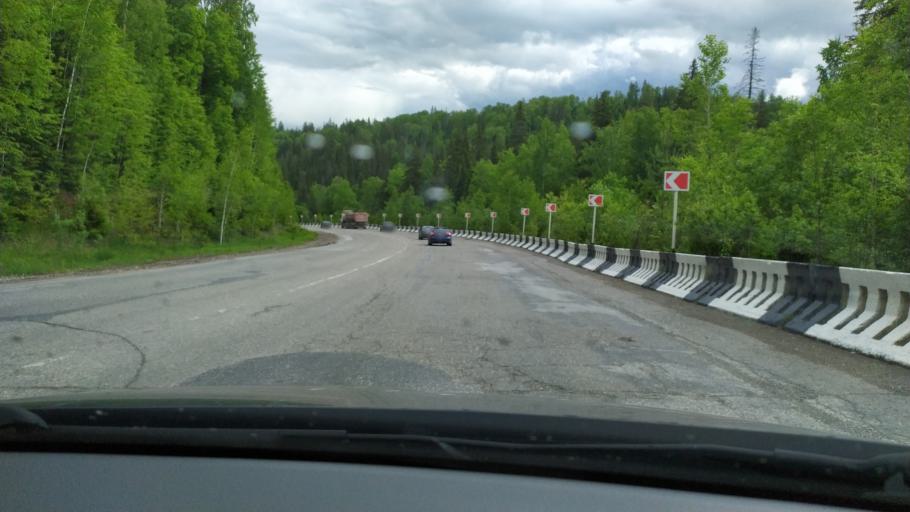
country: RU
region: Perm
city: Gremyachinsk
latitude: 58.4421
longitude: 57.8680
